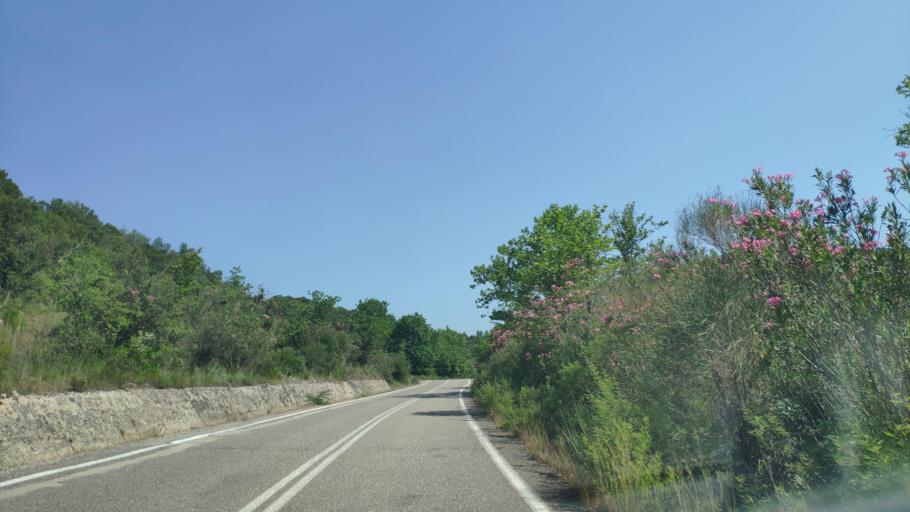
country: GR
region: West Greece
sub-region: Nomos Aitolias kai Akarnanias
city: Lepenou
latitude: 38.7761
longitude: 21.3350
